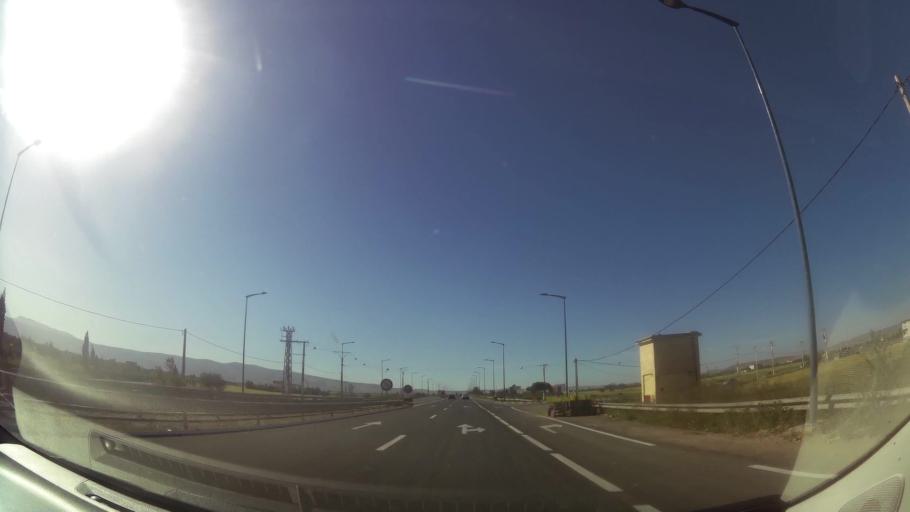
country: MA
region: Oriental
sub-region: Oujda-Angad
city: Oujda
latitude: 34.8242
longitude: -1.9699
